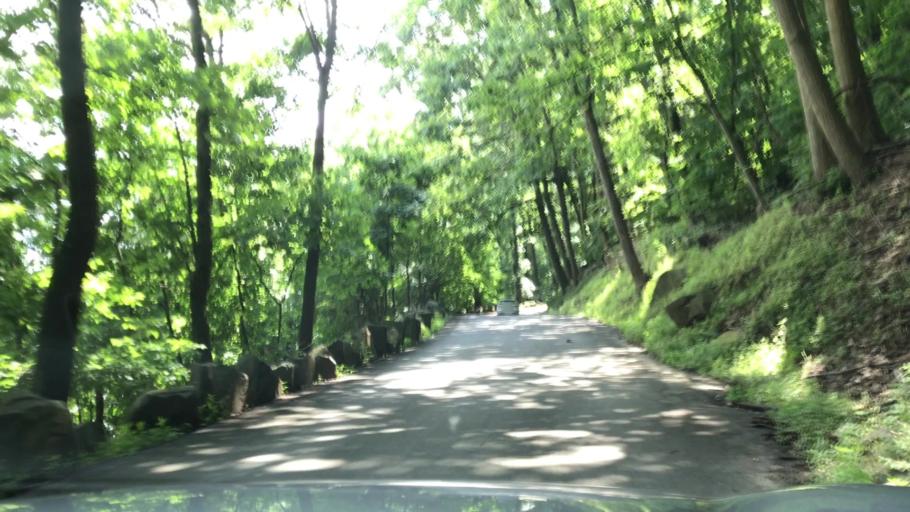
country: US
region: New Jersey
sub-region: Bergen County
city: Englewood Cliffs
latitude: 40.8846
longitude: -73.9431
